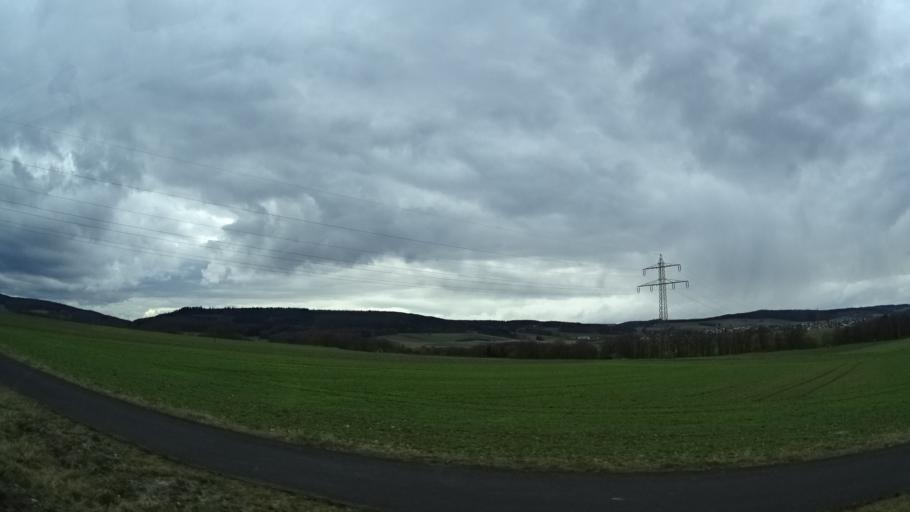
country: DE
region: Hesse
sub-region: Regierungsbezirk Kassel
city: Bad Salzschlirf
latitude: 50.6086
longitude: 9.5072
